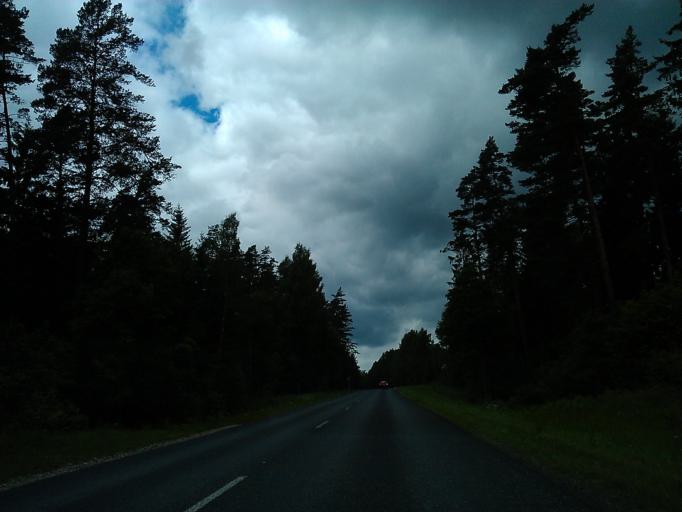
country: LV
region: Talsu Rajons
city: Stende
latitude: 57.0908
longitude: 22.3940
